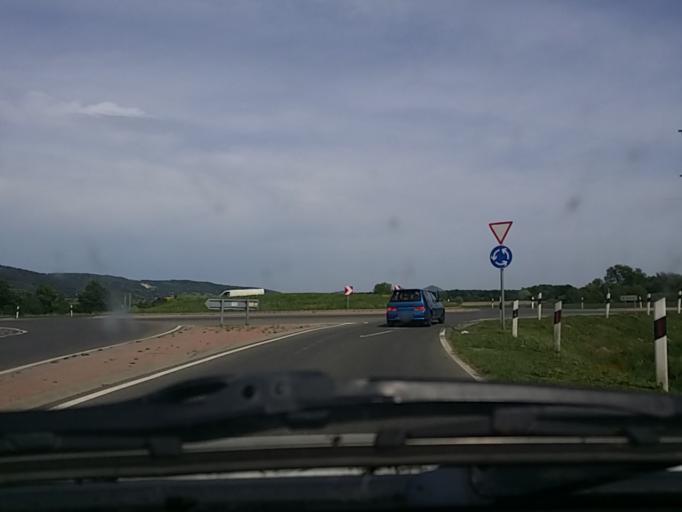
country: HU
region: Baranya
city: Harkany
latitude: 45.8642
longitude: 18.2323
